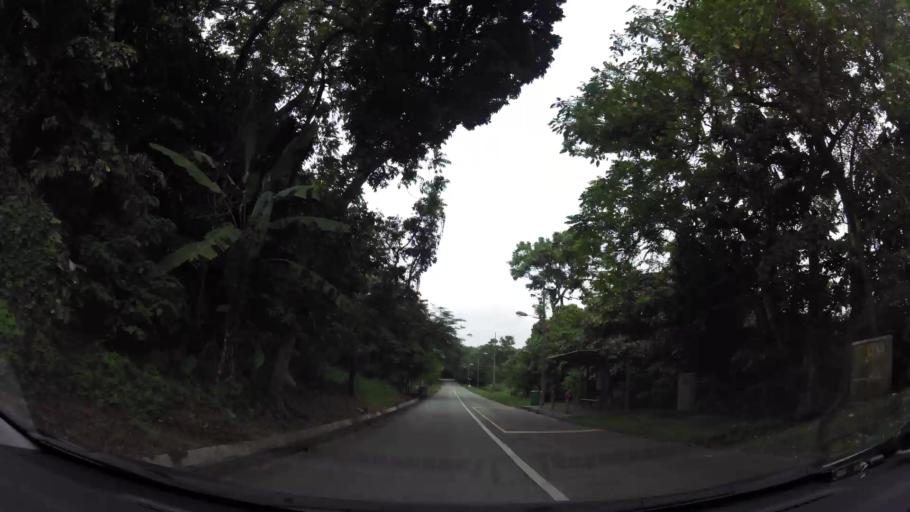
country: MY
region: Johor
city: Johor Bahru
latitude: 1.4425
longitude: 103.7078
